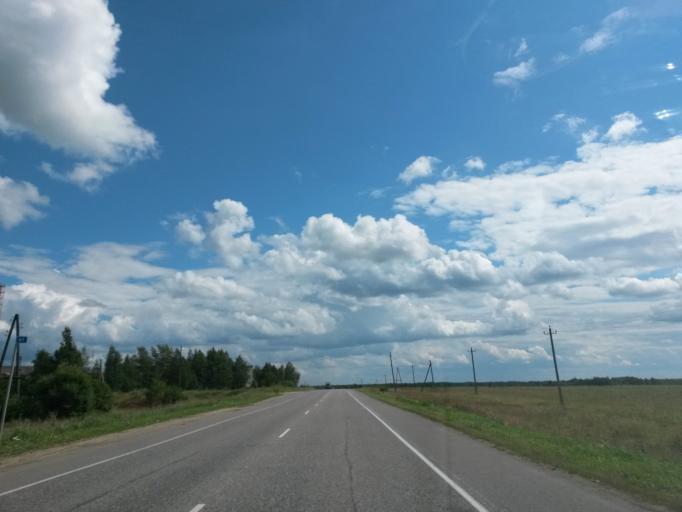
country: RU
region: Ivanovo
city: Pistsovo
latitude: 57.1729
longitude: 40.5077
